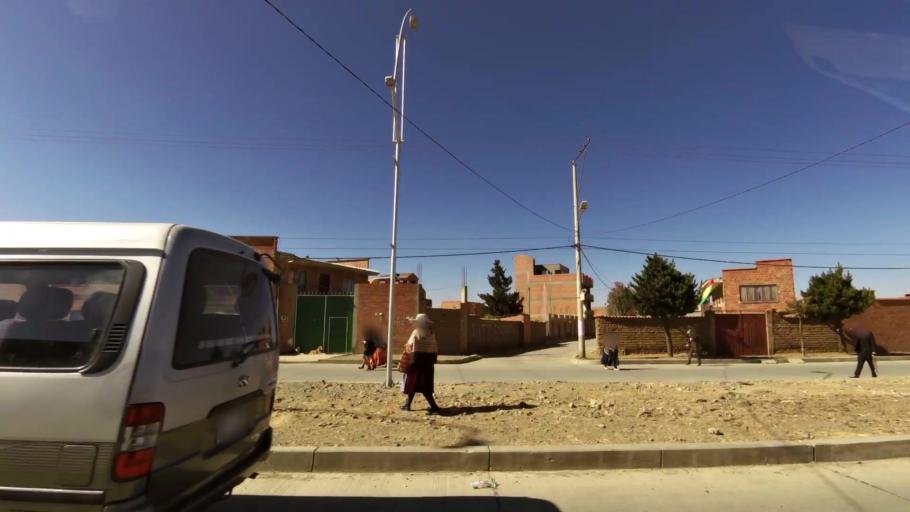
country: BO
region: La Paz
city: La Paz
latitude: -16.5318
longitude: -68.2230
